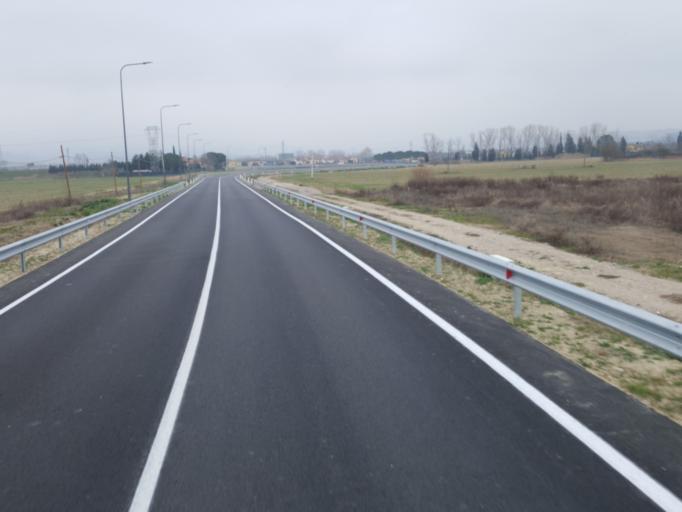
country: IT
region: Tuscany
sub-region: Province of Florence
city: Pozzale-Case Nuove
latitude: 43.7129
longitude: 10.9813
